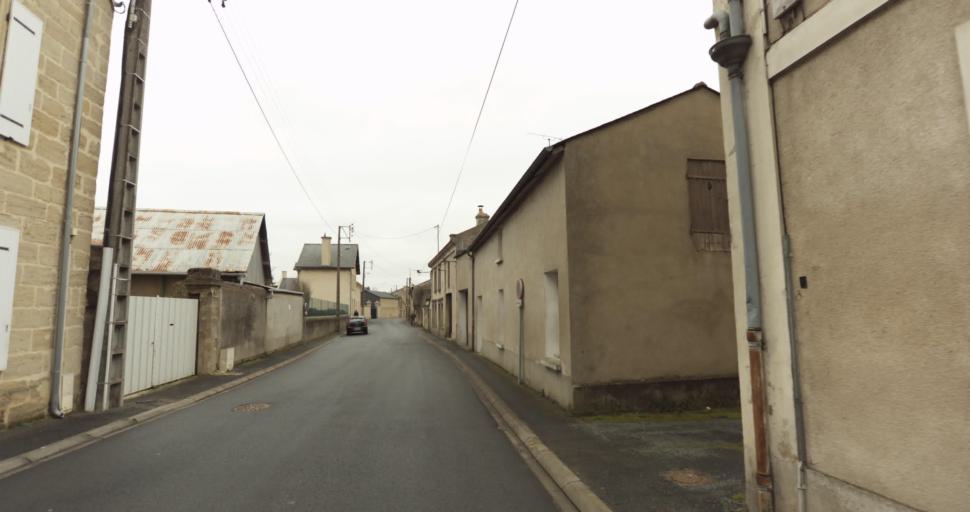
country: FR
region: Pays de la Loire
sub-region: Departement de Maine-et-Loire
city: Doue-la-Fontaine
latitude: 47.1897
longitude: -0.2684
